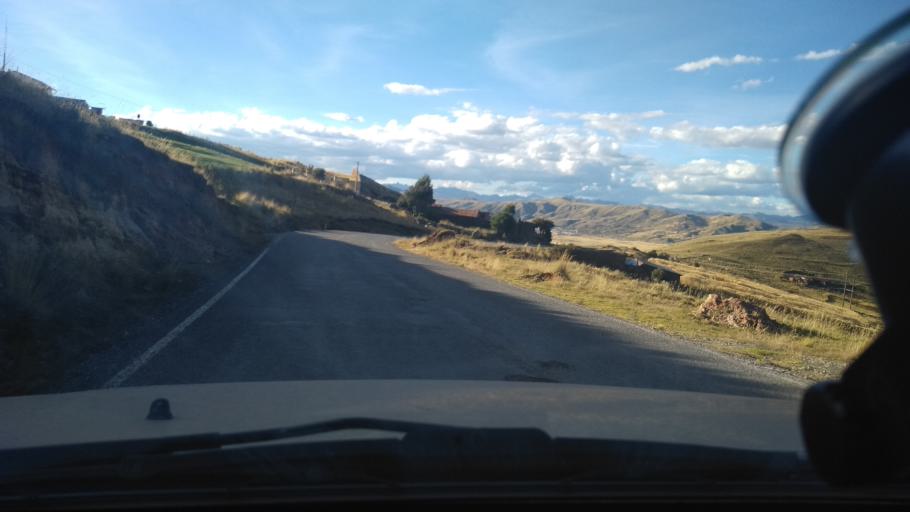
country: PE
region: Cusco
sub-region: Provincia de Canas
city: Ccaquiracunca
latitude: -14.2799
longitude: -71.4489
